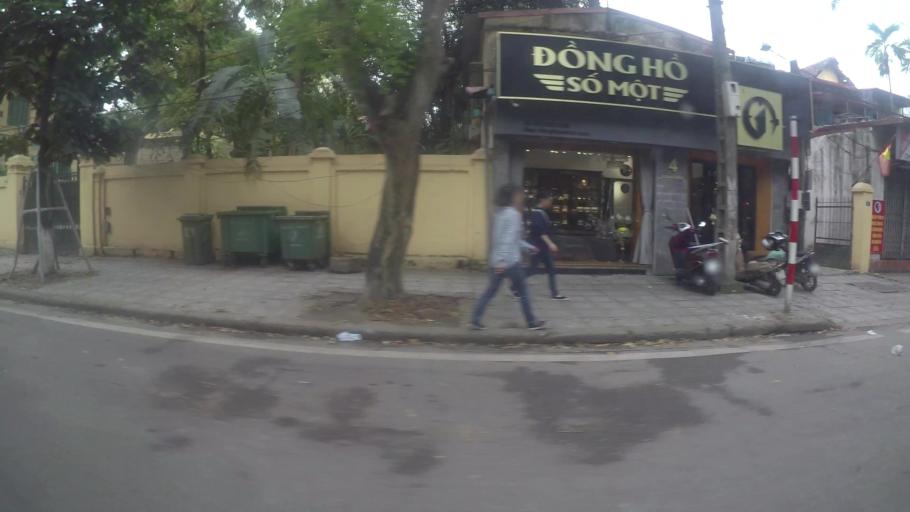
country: VN
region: Ha Noi
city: Hanoi
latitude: 21.0402
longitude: 105.8397
